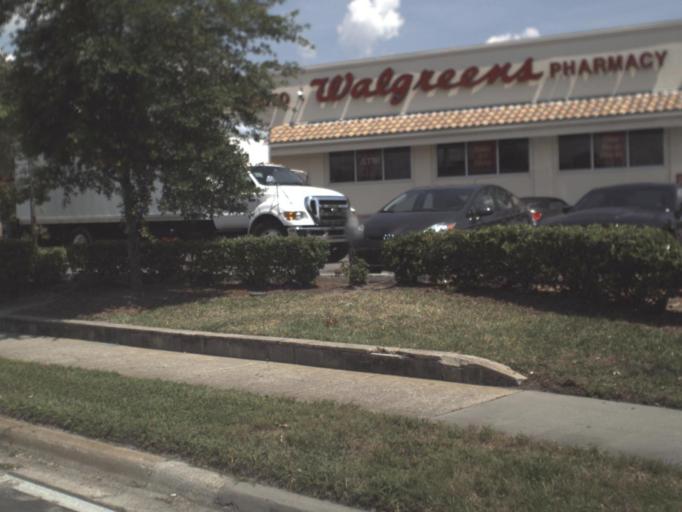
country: US
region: Florida
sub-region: Duval County
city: Jacksonville
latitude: 30.3473
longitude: -81.6666
